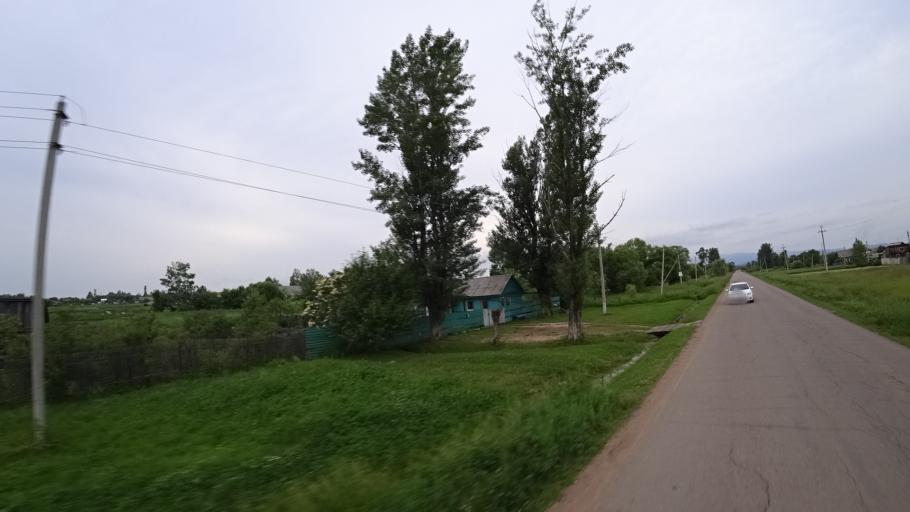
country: RU
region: Primorskiy
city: Novosysoyevka
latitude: 44.2351
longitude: 133.3701
